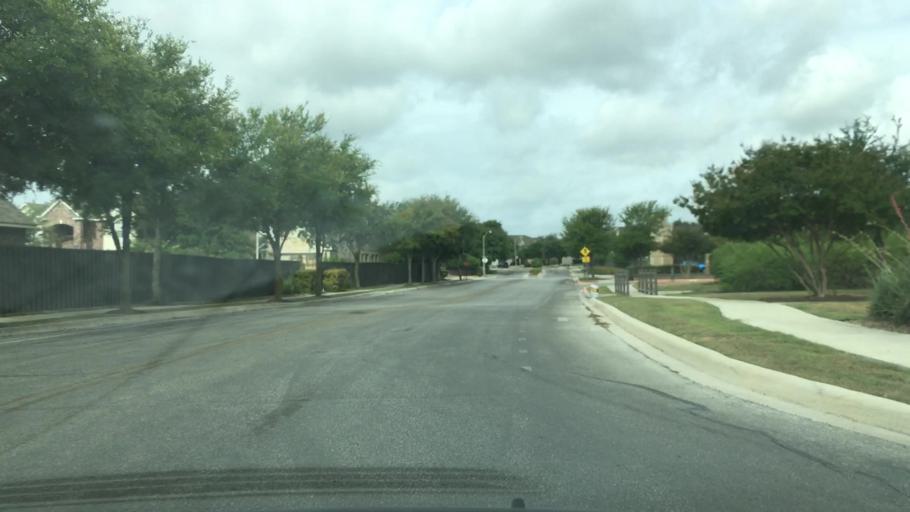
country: US
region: Texas
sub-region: Guadalupe County
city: Cibolo
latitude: 29.5828
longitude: -98.2452
